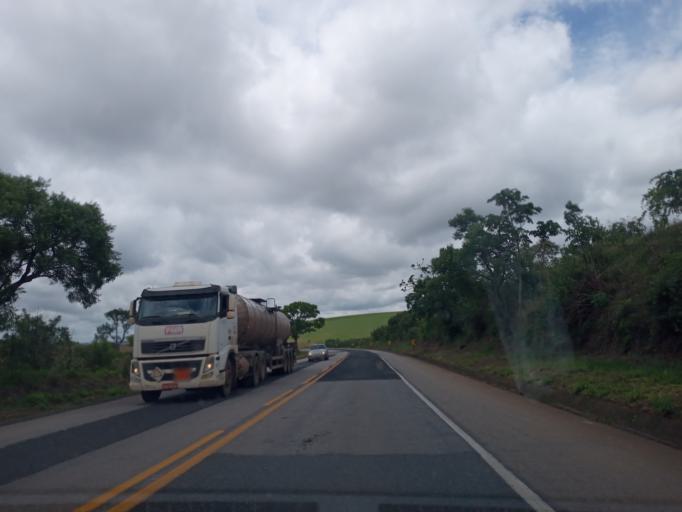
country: BR
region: Minas Gerais
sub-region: Ibia
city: Ibia
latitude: -19.5769
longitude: -46.5315
